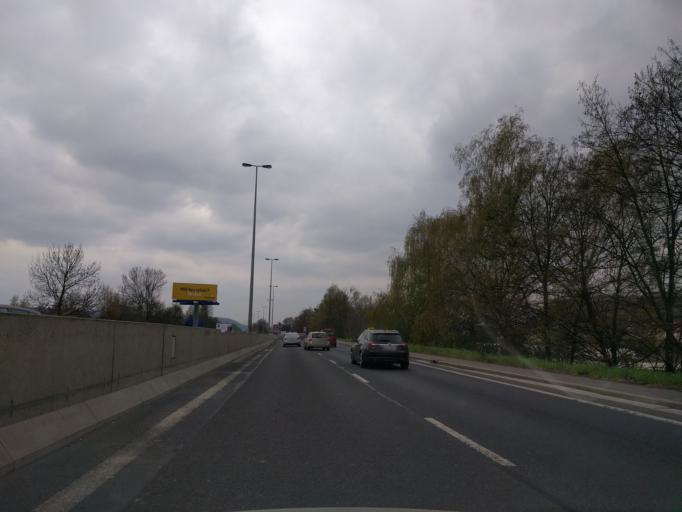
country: CZ
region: Praha
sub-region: Praha 12
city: Modrany
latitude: 50.0155
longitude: 14.3940
